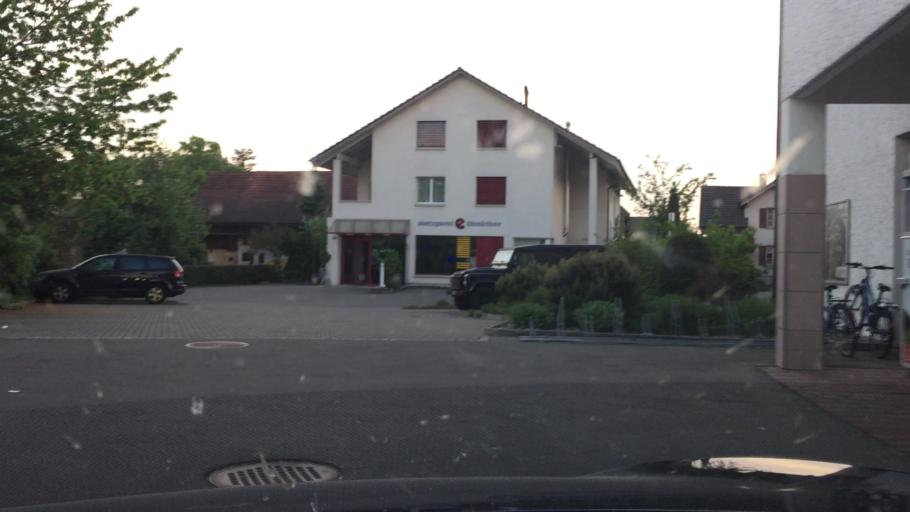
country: CH
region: Thurgau
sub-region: Frauenfeld District
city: Mullheim
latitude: 47.6015
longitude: 9.0008
